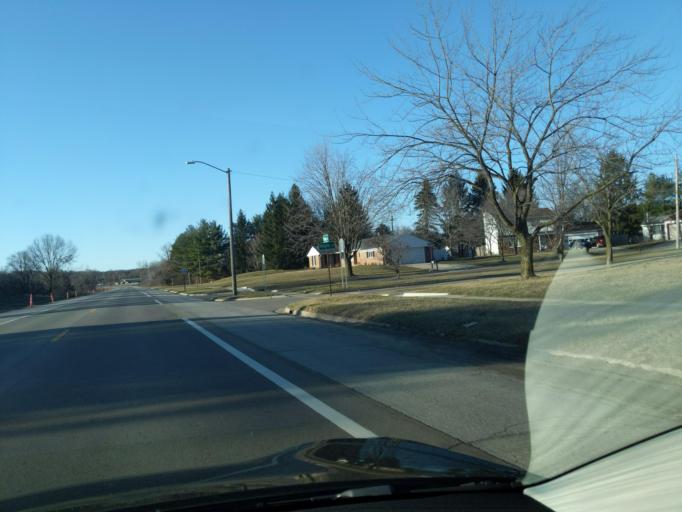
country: US
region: Michigan
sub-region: Washtenaw County
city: Chelsea
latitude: 42.3292
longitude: -84.0232
